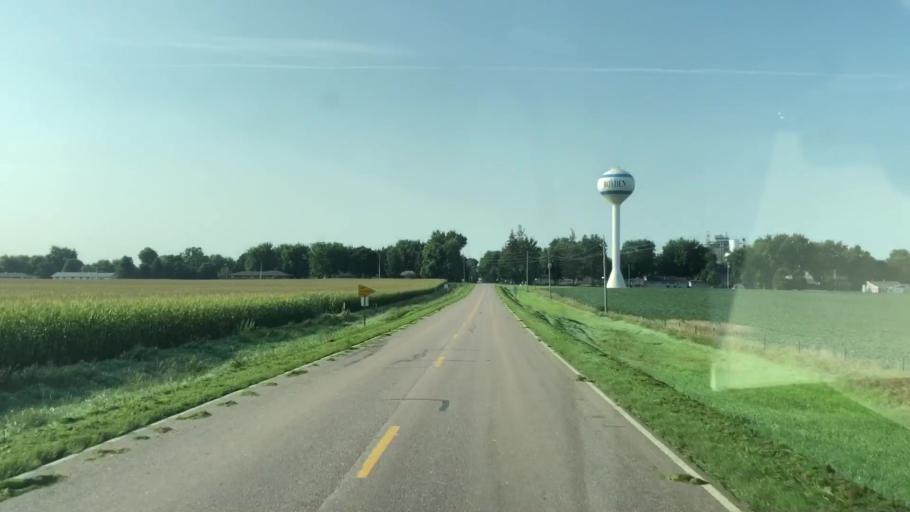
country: US
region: Iowa
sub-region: Sioux County
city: Hull
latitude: 43.1963
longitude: -96.0004
